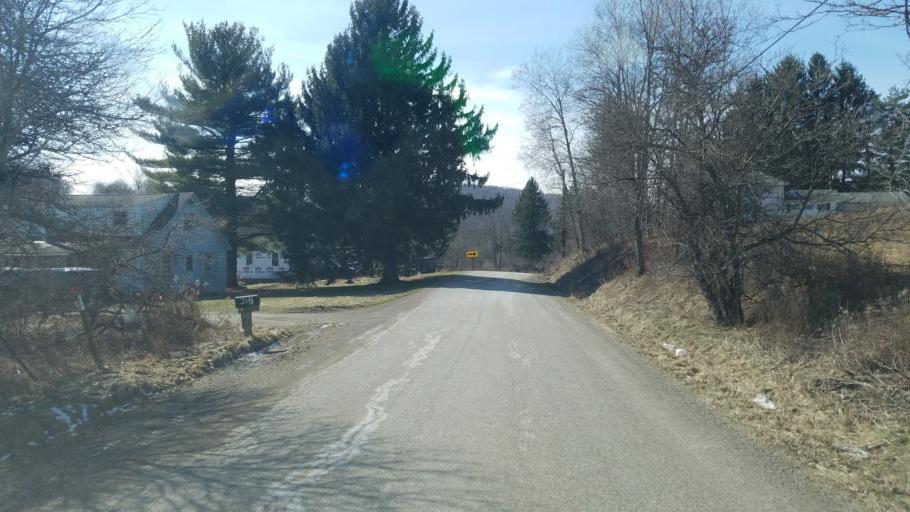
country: US
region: New York
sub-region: Allegany County
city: Andover
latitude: 41.9475
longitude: -77.8074
